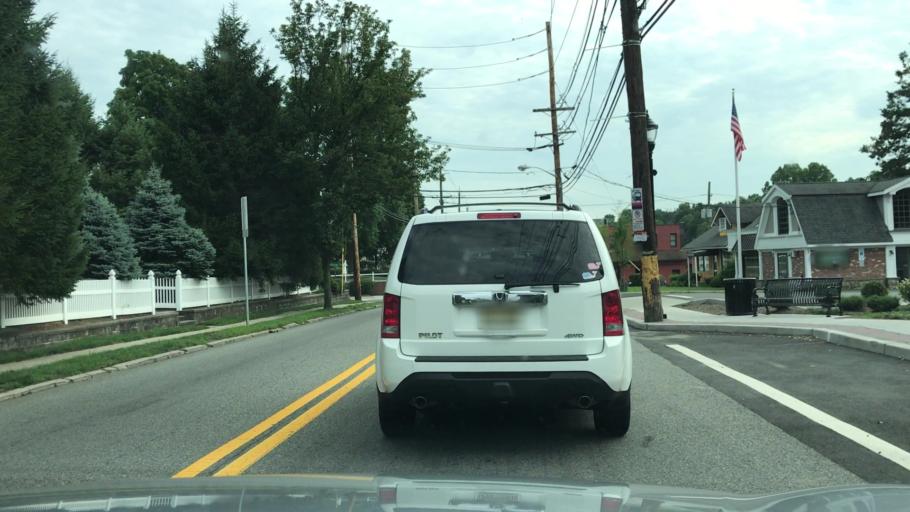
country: US
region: New Jersey
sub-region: Bergen County
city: Emerson
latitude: 40.9776
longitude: -74.0255
